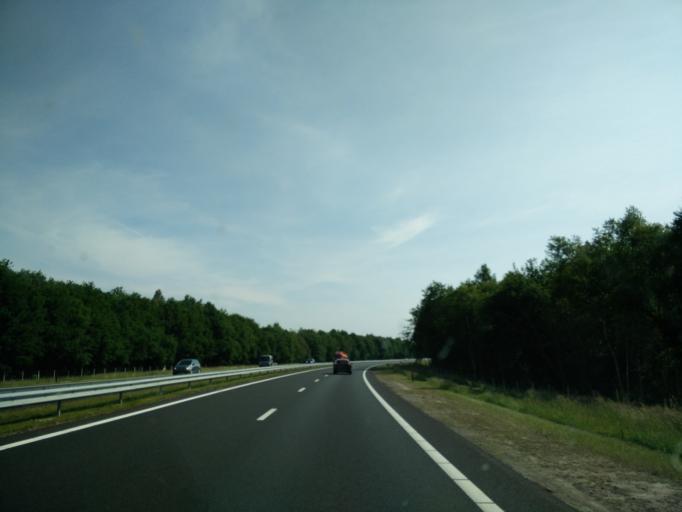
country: NL
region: Drenthe
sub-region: Gemeente Aa en Hunze
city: Anloo
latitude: 52.9969
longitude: 6.6961
